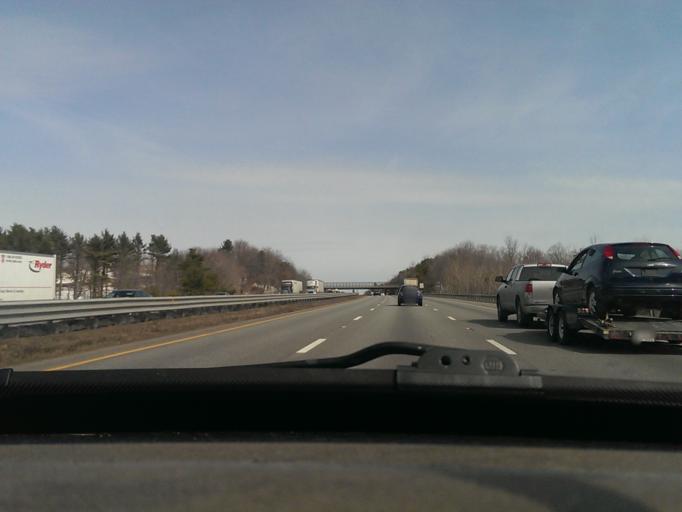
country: US
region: Massachusetts
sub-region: Worcester County
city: Leicester
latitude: 42.1768
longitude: -71.9114
